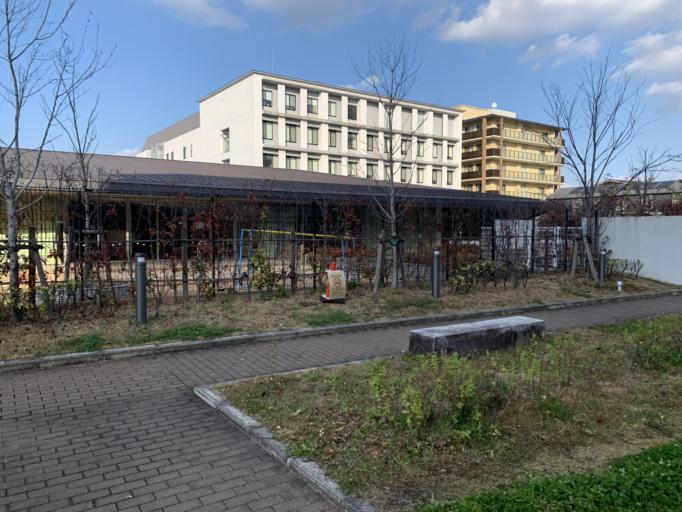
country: JP
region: Kyoto
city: Kyoto
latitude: 34.9976
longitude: 135.7347
